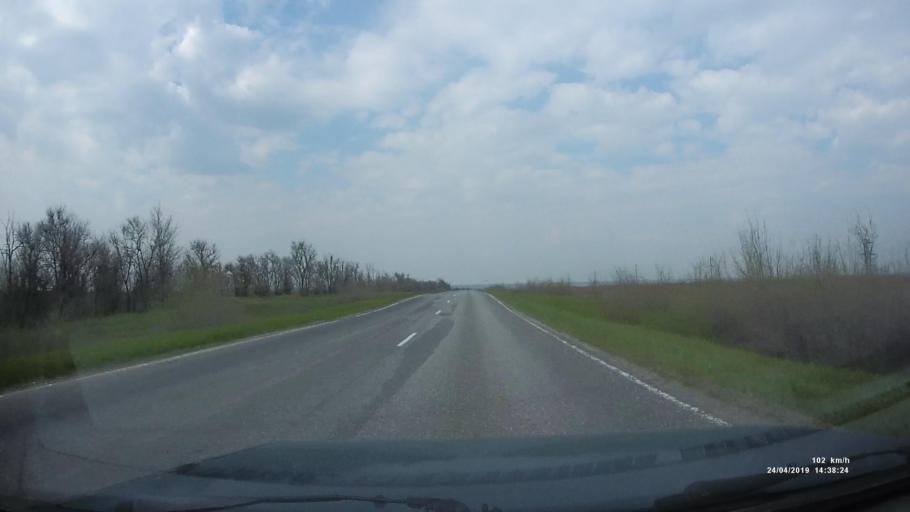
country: RU
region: Rostov
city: Remontnoye
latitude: 46.4009
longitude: 43.8861
